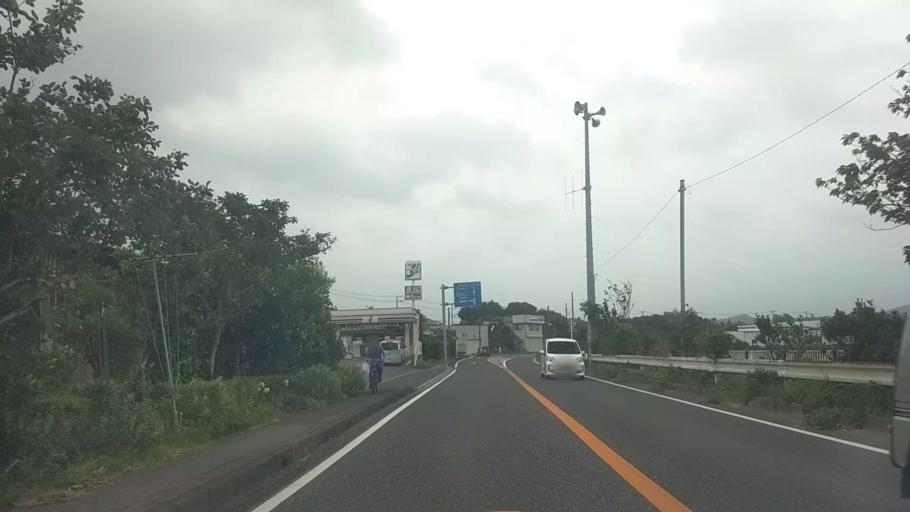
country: JP
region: Chiba
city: Kimitsu
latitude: 35.2184
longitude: 139.8884
